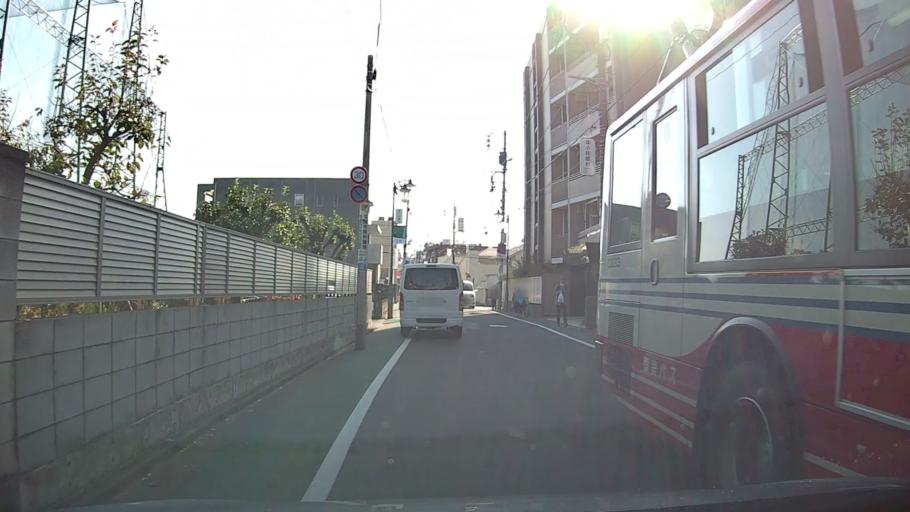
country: JP
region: Tokyo
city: Musashino
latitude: 35.7301
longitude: 139.5916
